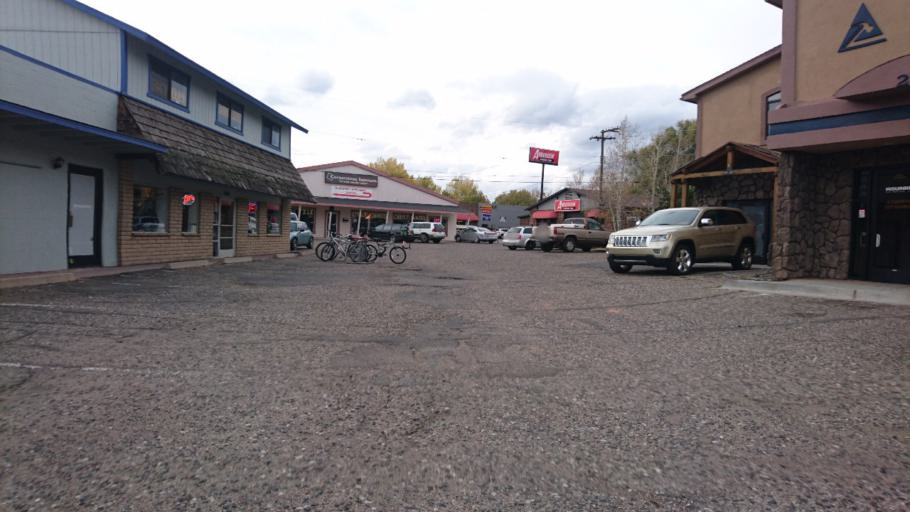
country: US
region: Arizona
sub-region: Coconino County
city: Flagstaff
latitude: 35.2061
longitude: -111.6136
